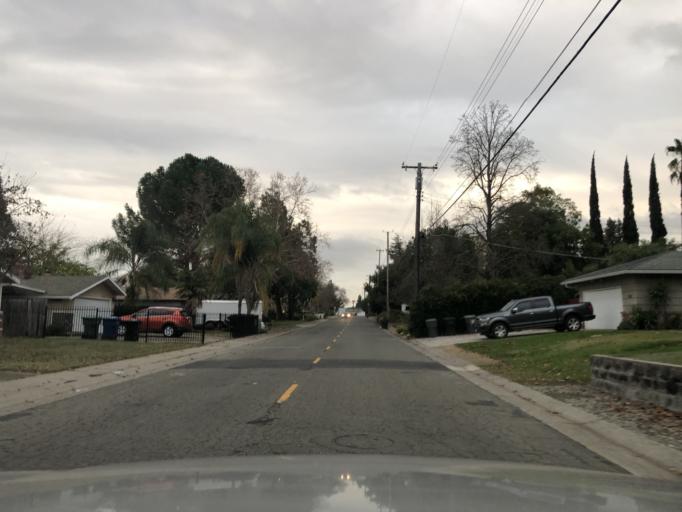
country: US
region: California
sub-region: Sacramento County
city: Foothill Farms
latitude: 38.6627
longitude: -121.3151
